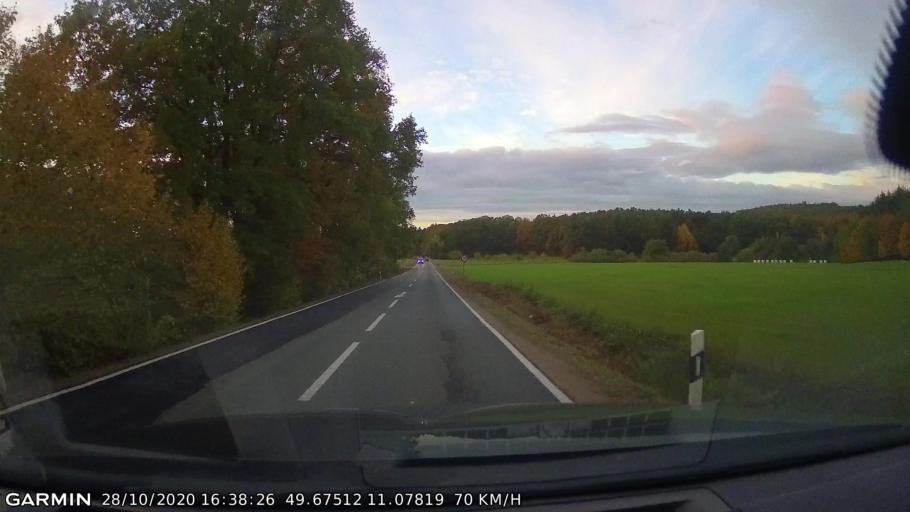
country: DE
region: Bavaria
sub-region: Upper Franconia
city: Poxdorf
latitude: 49.6752
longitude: 11.0781
